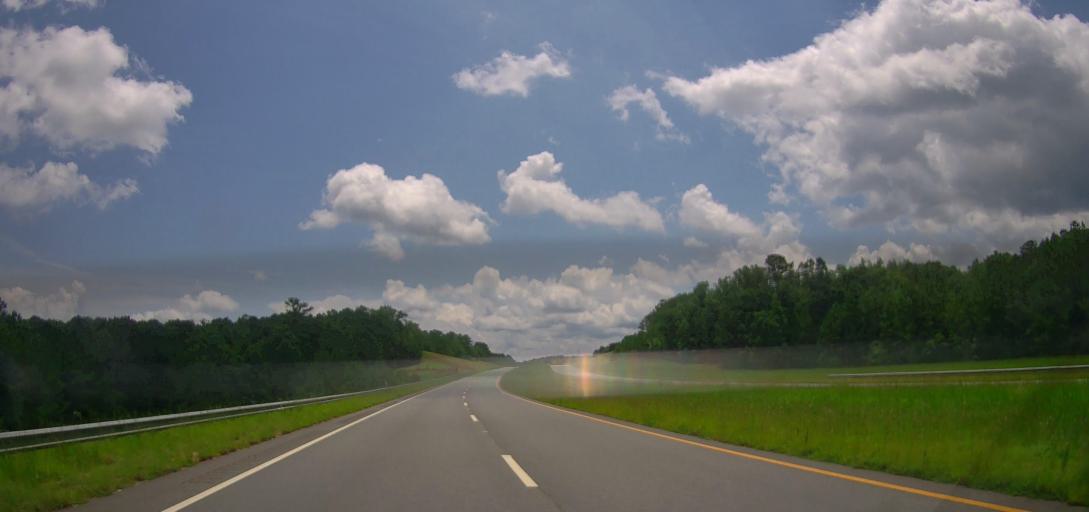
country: US
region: Georgia
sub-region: Upson County
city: Thomaston
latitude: 32.8368
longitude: -84.3096
